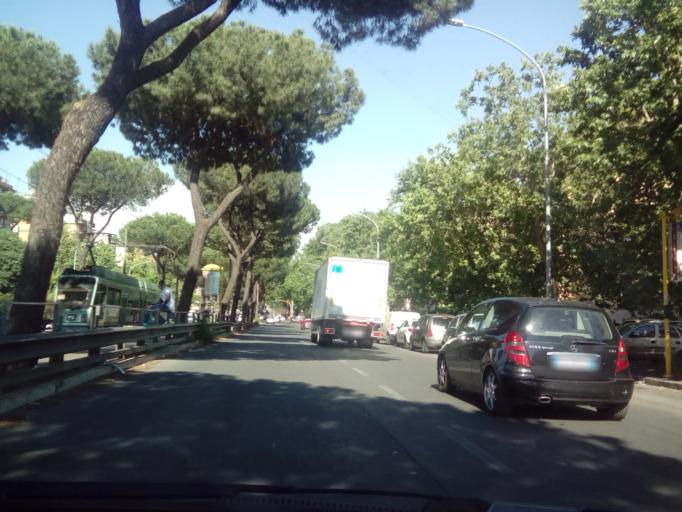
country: IT
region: Latium
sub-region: Citta metropolitana di Roma Capitale
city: Rome
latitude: 41.8942
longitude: 12.5552
